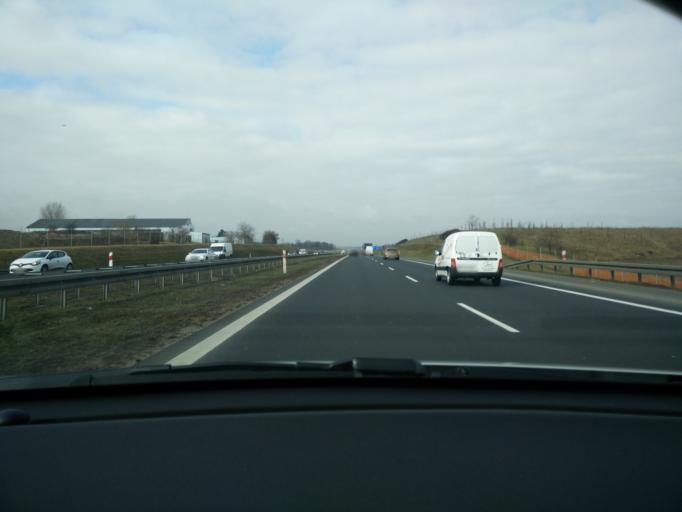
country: PL
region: Greater Poland Voivodeship
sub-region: Powiat poznanski
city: Daszewice
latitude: 52.3495
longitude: 16.9586
